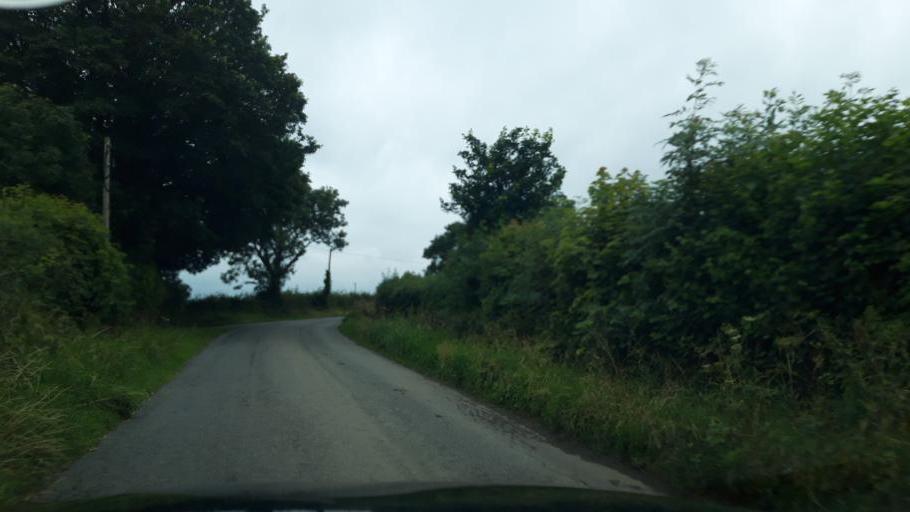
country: IE
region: Leinster
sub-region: Kilkenny
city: Ballyragget
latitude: 52.7013
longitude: -7.4099
